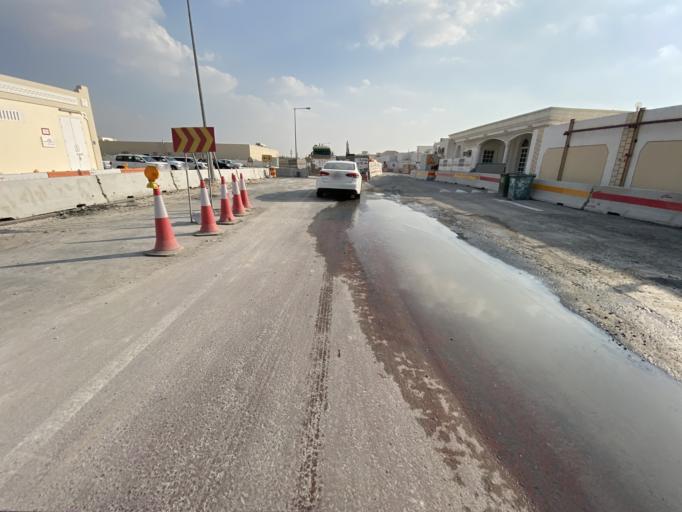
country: QA
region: Baladiyat ar Rayyan
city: Ar Rayyan
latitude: 25.2319
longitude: 51.3791
